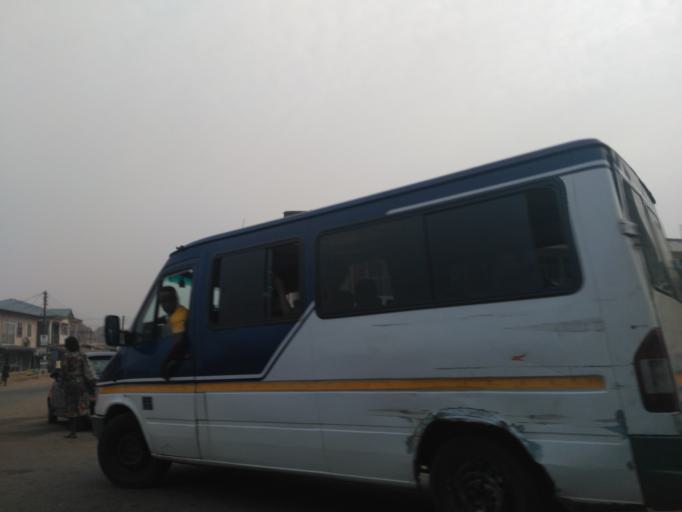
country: GH
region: Greater Accra
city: Dome
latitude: 5.6584
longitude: -0.2663
